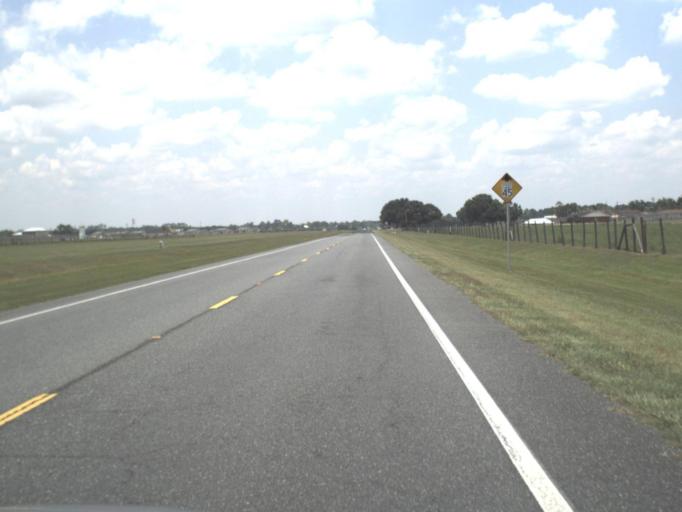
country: US
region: Florida
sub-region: Bradford County
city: Starke
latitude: 30.0556
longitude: -82.1763
